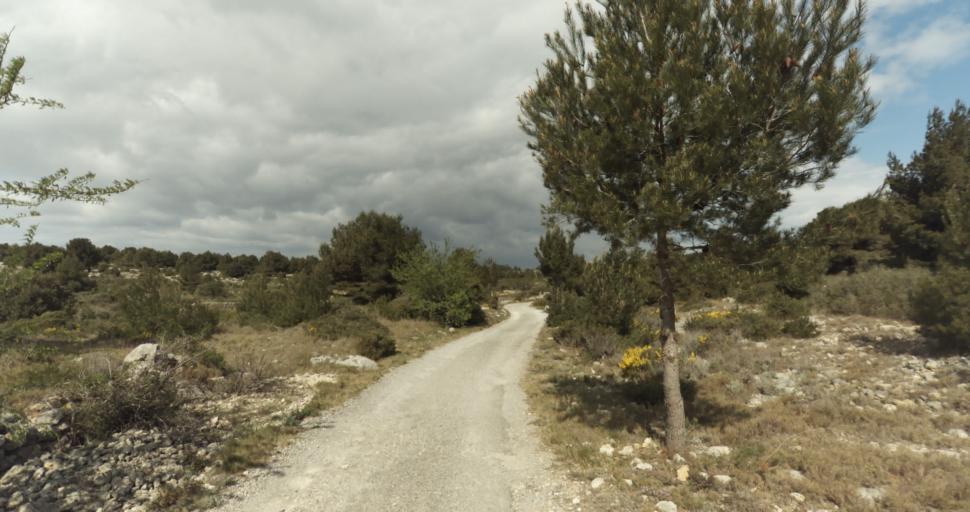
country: FR
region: Languedoc-Roussillon
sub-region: Departement de l'Aude
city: Leucate
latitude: 42.9192
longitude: 3.0489
